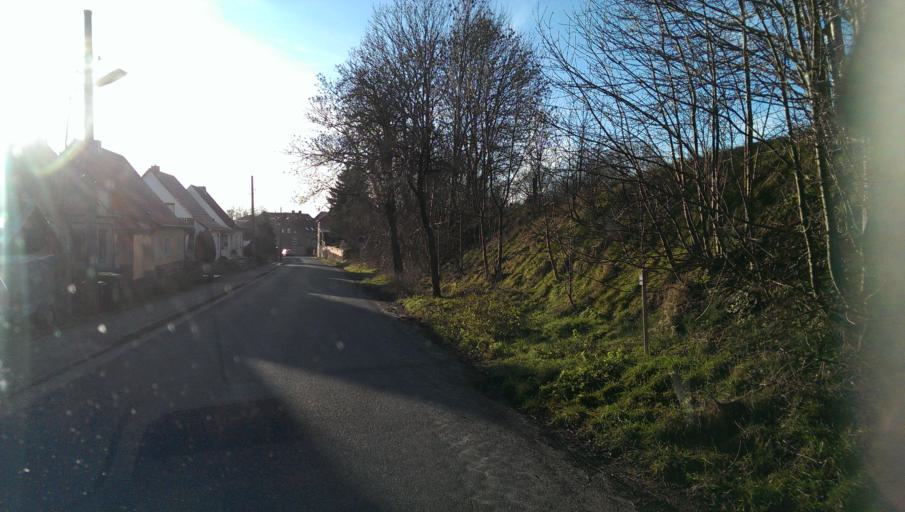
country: DE
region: Saxony-Anhalt
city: Ausleben
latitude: 52.0941
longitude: 11.1601
